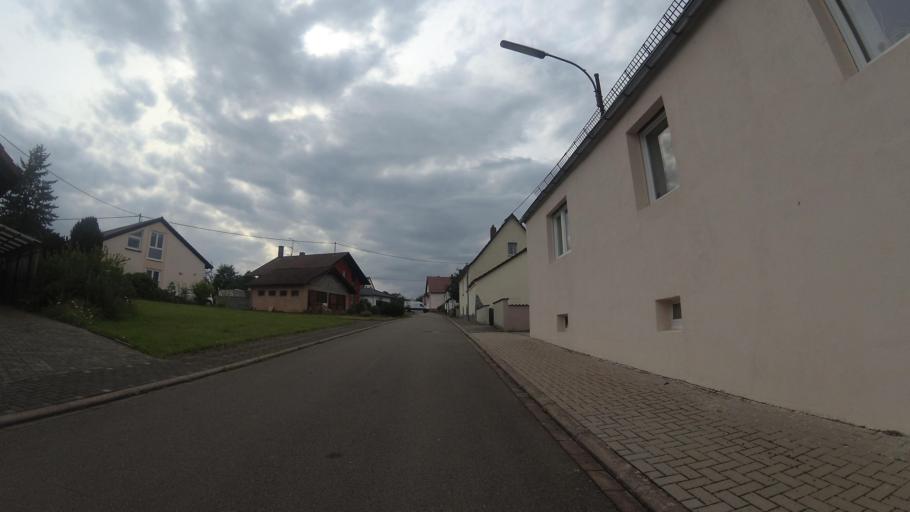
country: DE
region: Rheinland-Pfalz
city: Selchenbach
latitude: 49.4976
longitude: 7.2950
